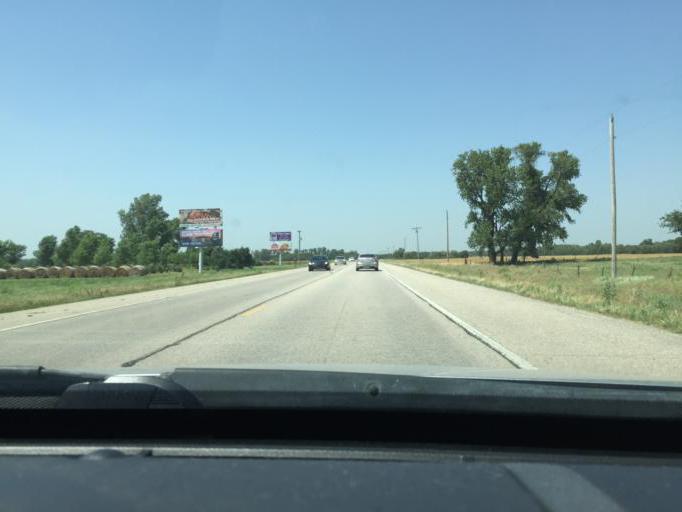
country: US
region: Kansas
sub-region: Reno County
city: South Hutchinson
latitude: 37.9926
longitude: -97.8669
